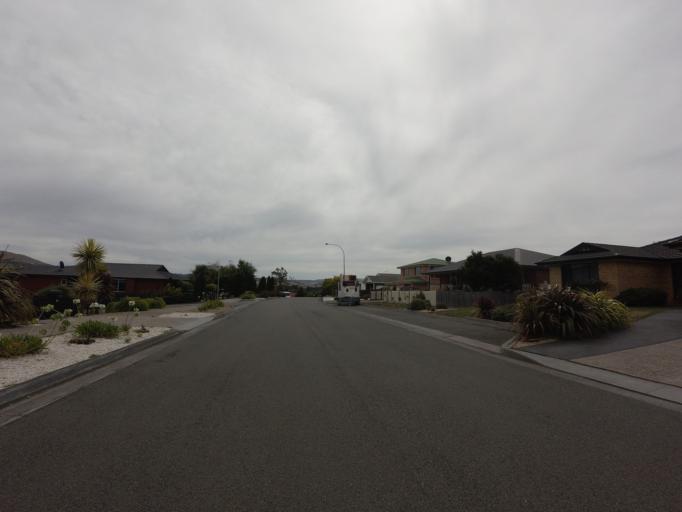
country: AU
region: Tasmania
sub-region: Sorell
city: Sorell
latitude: -42.7842
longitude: 147.5246
